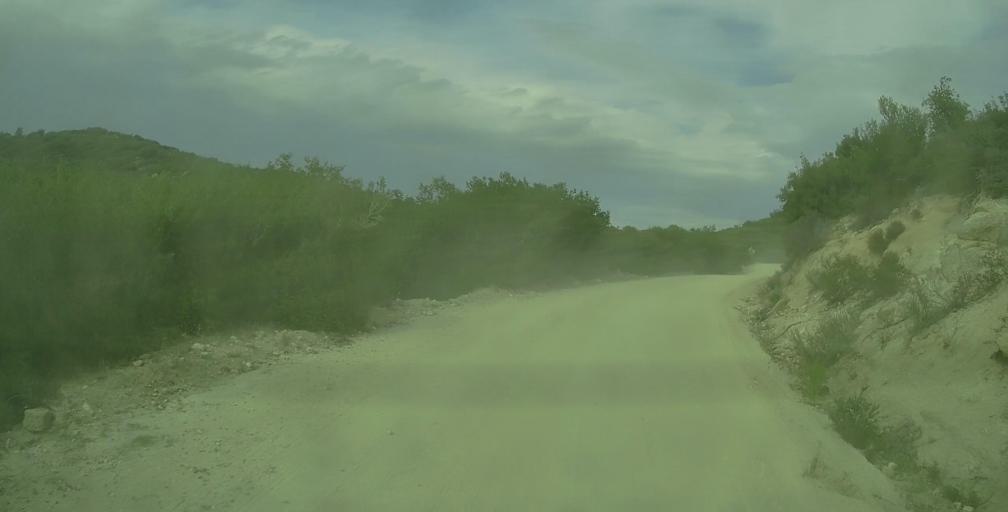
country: GR
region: Central Macedonia
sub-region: Nomos Chalkidikis
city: Sykia
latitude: 39.9921
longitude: 23.9156
